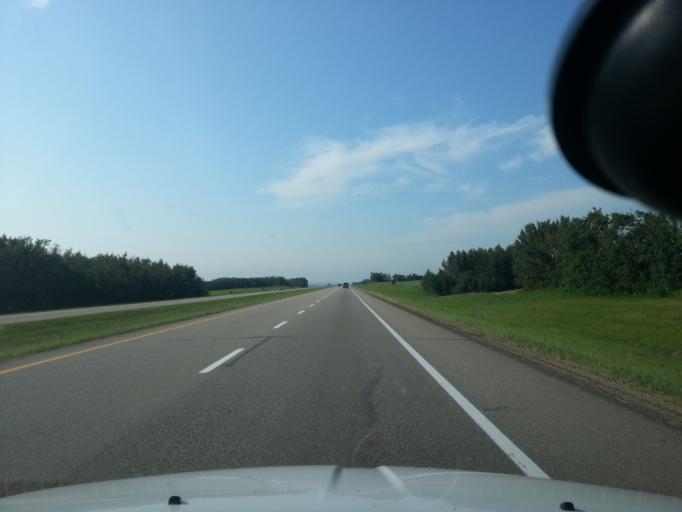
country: CA
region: Alberta
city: Ponoka
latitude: 52.7177
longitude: -113.6441
